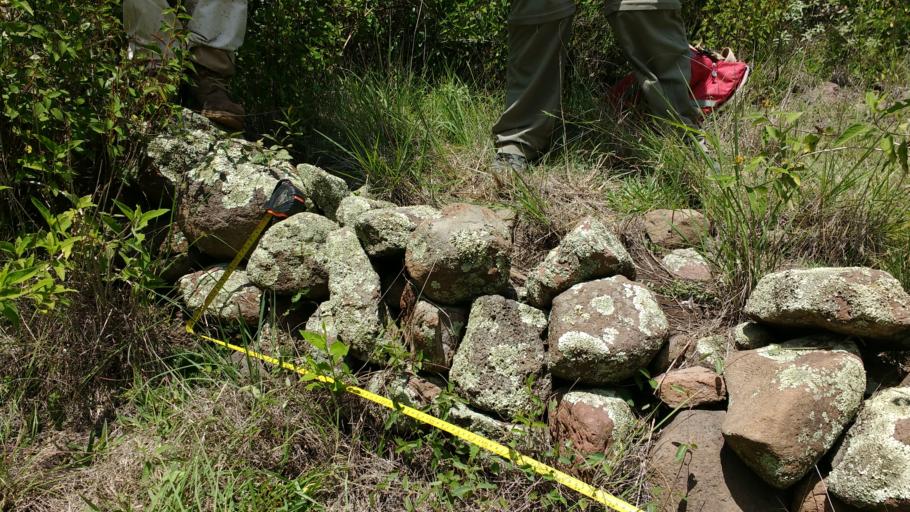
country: MX
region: Hidalgo
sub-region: Tezontepec de Aldama
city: Tenango
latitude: 20.2400
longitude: -99.2753
